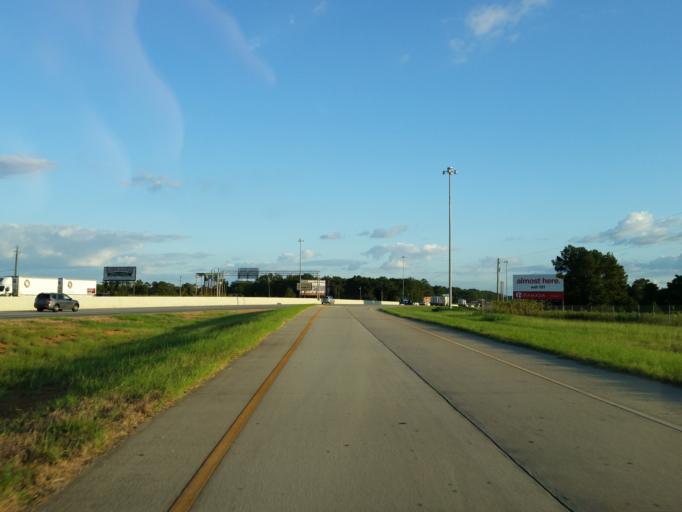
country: US
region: Georgia
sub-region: Crisp County
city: Cordele
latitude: 32.0010
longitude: -83.7587
